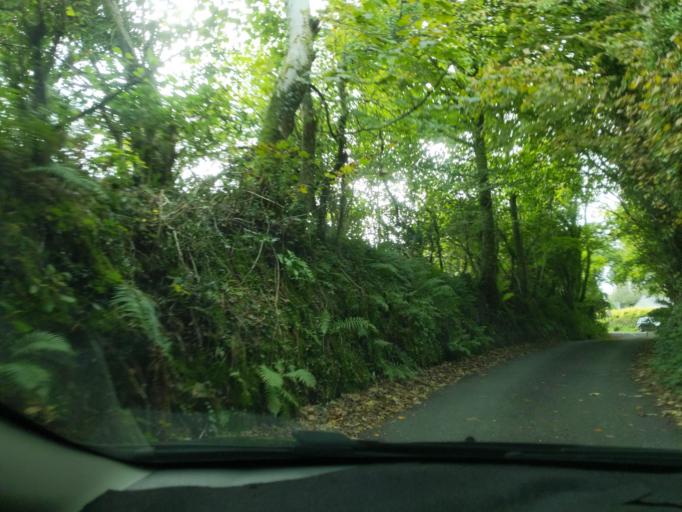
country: GB
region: England
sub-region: Cornwall
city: Lostwithiel
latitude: 50.4002
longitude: -4.7009
